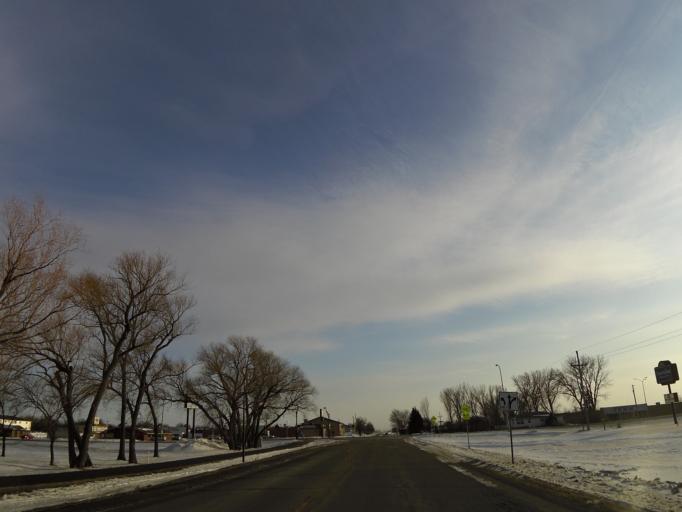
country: US
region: North Dakota
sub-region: Walsh County
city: Grafton
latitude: 48.4135
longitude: -97.4267
